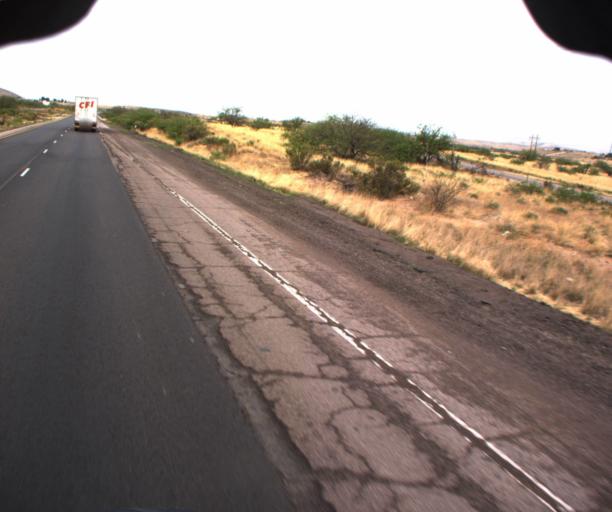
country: US
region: Arizona
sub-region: Cochise County
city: Mescal
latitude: 31.9631
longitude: -110.4411
